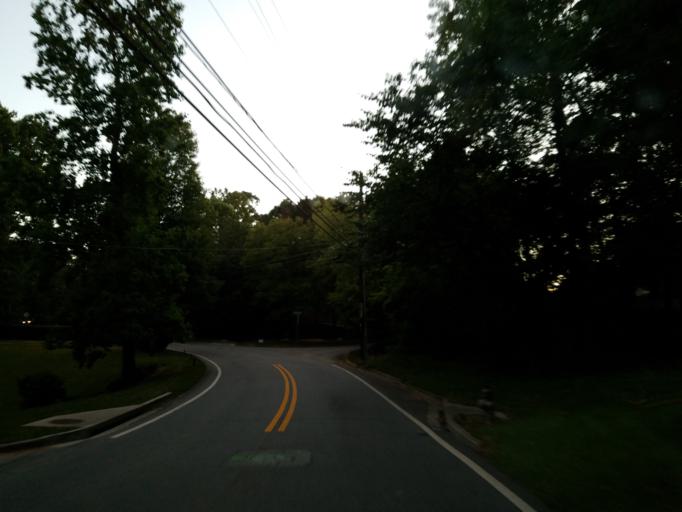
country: US
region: Georgia
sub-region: Fulton County
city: Sandy Springs
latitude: 33.8868
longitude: -84.4025
